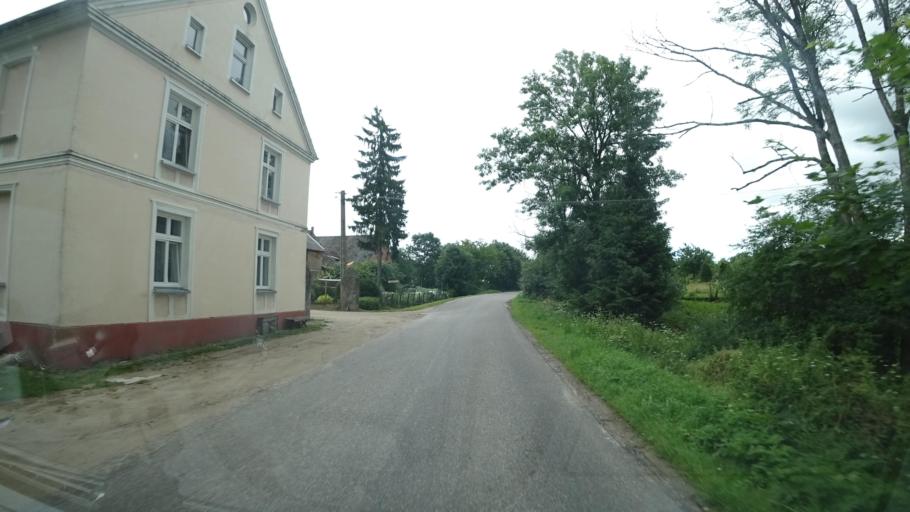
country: PL
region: Podlasie
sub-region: Powiat suwalski
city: Filipow
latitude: 54.2890
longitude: 22.5123
